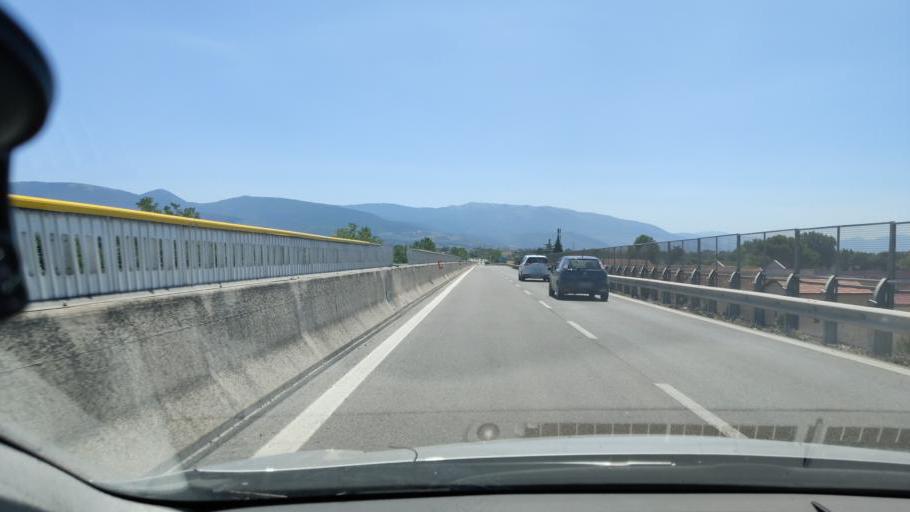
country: IT
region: Umbria
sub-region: Provincia di Perugia
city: Spello
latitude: 42.9855
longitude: 12.6698
